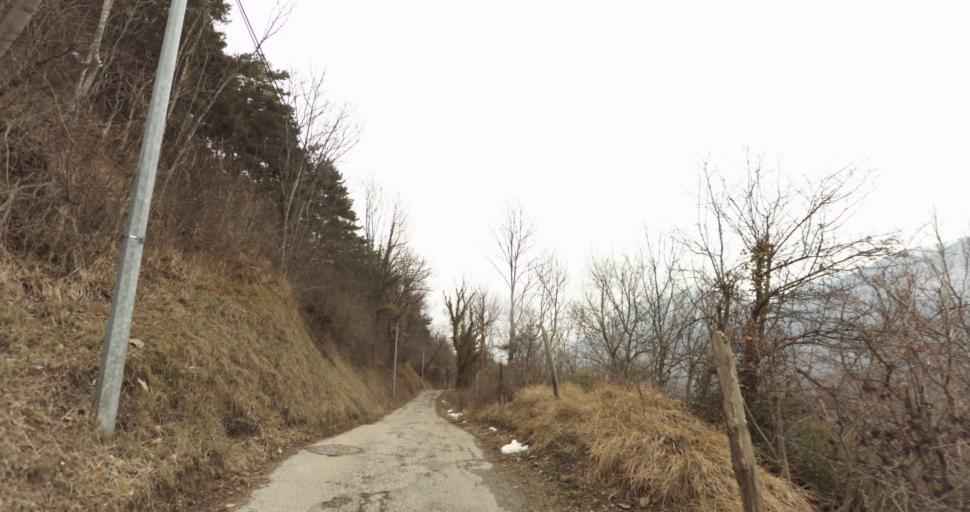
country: FR
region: Rhone-Alpes
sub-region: Departement de l'Isere
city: Saint-Georges-de-Commiers
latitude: 45.0075
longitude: 5.6797
